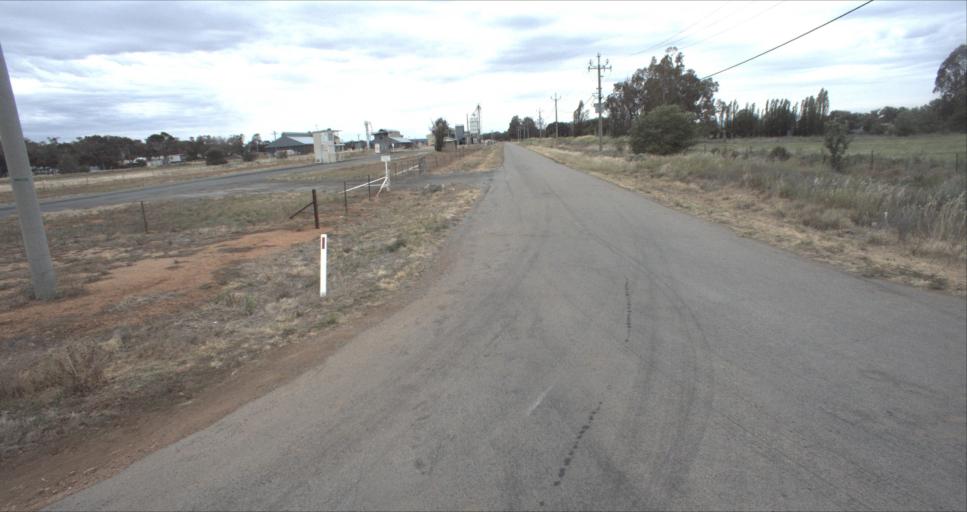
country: AU
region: New South Wales
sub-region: Leeton
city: Leeton
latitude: -34.4277
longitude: 146.3003
